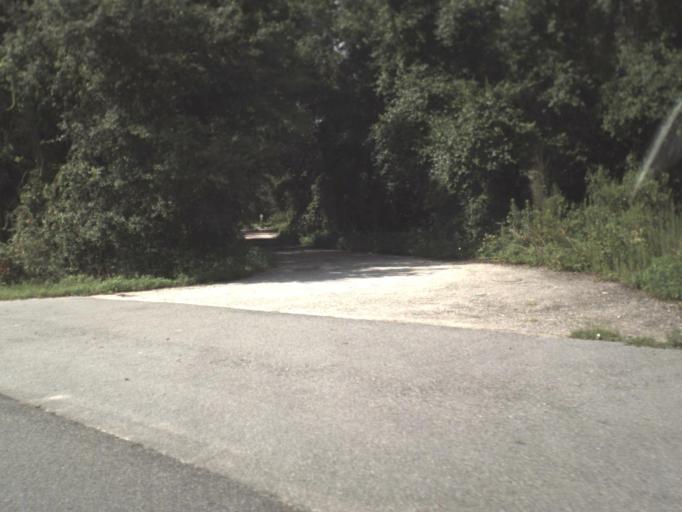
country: US
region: Florida
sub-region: Citrus County
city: Hernando
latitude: 28.9315
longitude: -82.3943
